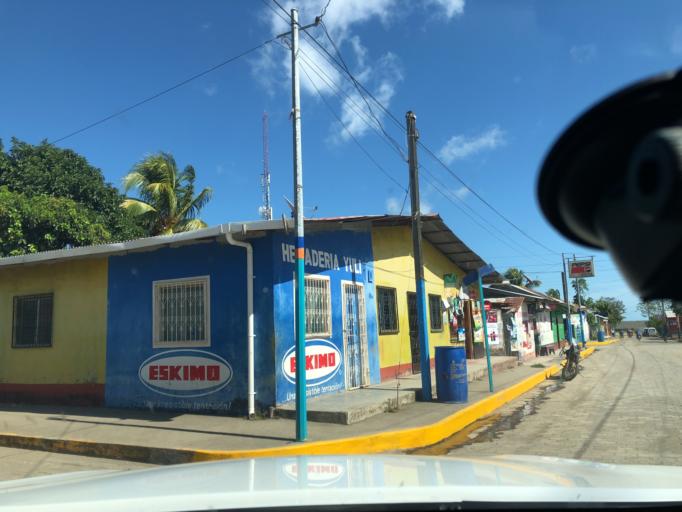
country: NI
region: Rivas
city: Cardenas
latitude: 11.1959
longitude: -85.5096
